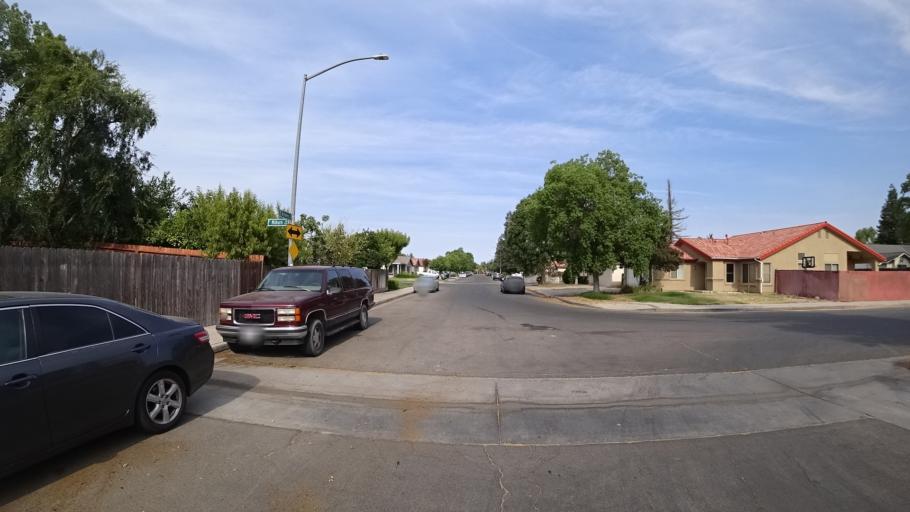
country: US
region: California
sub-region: Fresno County
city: West Park
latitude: 36.7697
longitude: -119.8757
